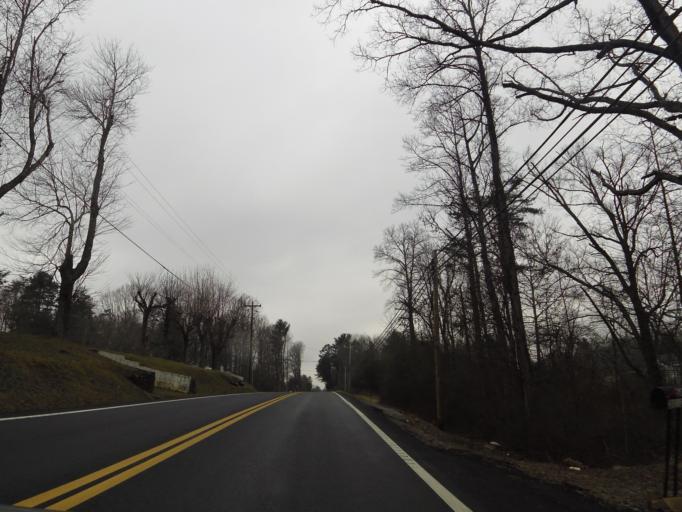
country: US
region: Tennessee
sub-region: Morgan County
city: Wartburg
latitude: 36.0865
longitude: -84.5605
